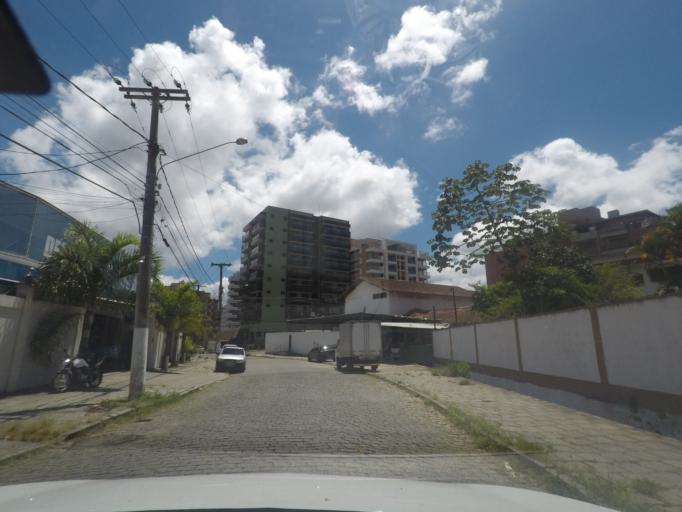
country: BR
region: Rio de Janeiro
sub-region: Teresopolis
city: Teresopolis
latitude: -22.4218
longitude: -42.9805
